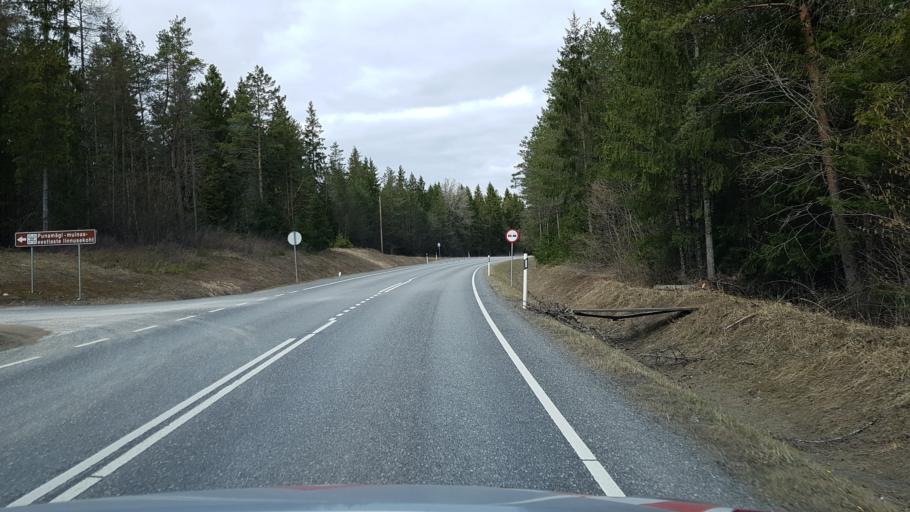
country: EE
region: Laeaene-Virumaa
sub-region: Rakke vald
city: Rakke
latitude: 59.0525
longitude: 26.2351
